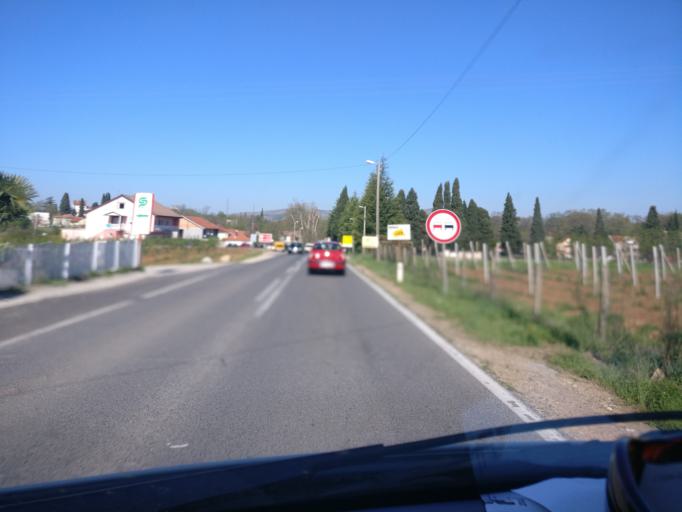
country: BA
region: Federation of Bosnia and Herzegovina
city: Tasovcici
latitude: 43.1370
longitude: 17.7833
